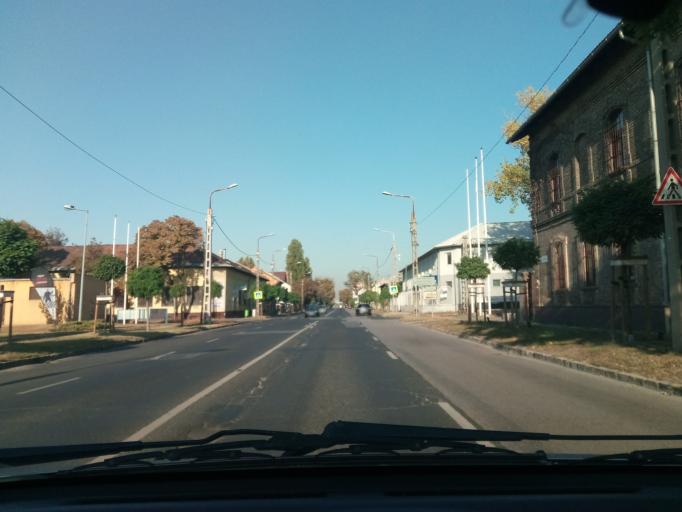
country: HU
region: Budapest
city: Budapest X. keruelet
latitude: 47.4697
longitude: 19.1462
